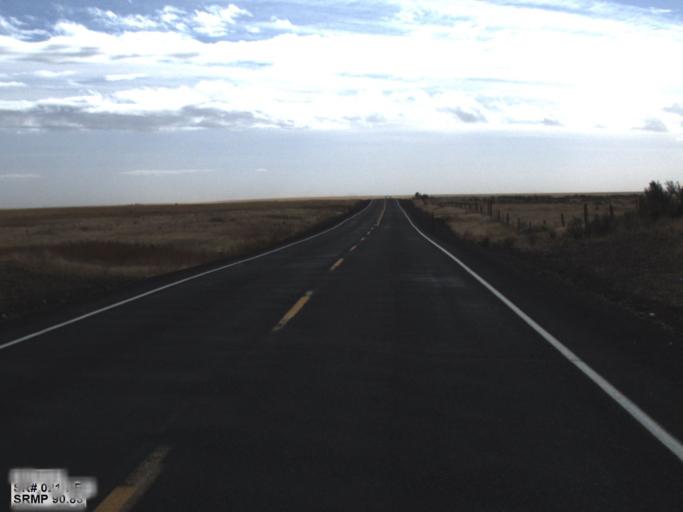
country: US
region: Washington
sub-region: Okanogan County
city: Coulee Dam
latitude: 47.7534
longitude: -118.7217
